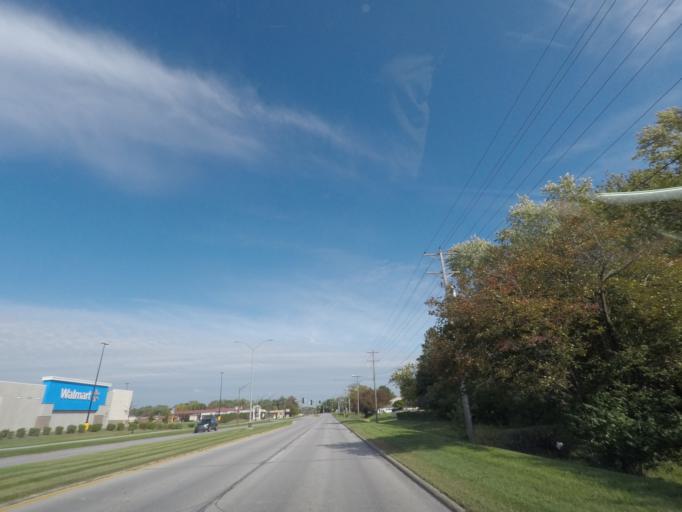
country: US
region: Iowa
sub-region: Story County
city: Ames
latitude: 42.0525
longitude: -93.6205
